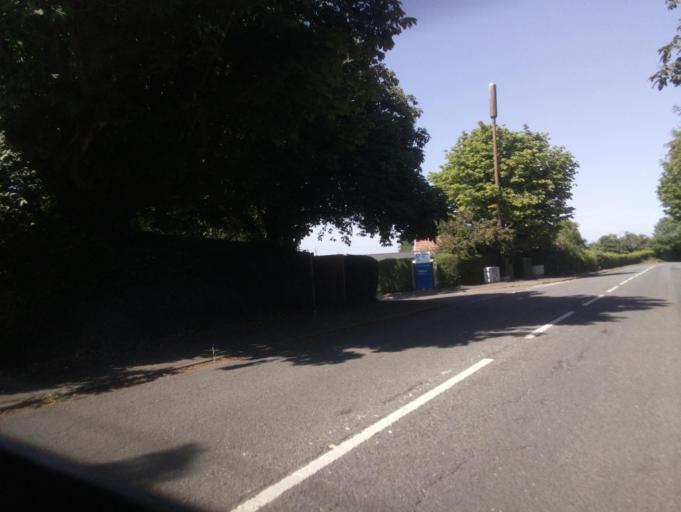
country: GB
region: England
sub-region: Borough of Torbay
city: Paignton
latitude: 50.4142
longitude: -3.5686
